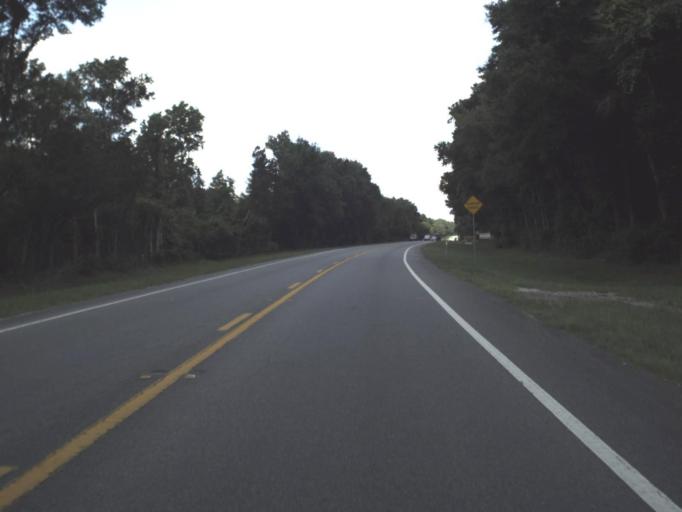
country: US
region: Florida
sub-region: Alachua County
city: High Springs
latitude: 29.8398
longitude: -82.6260
